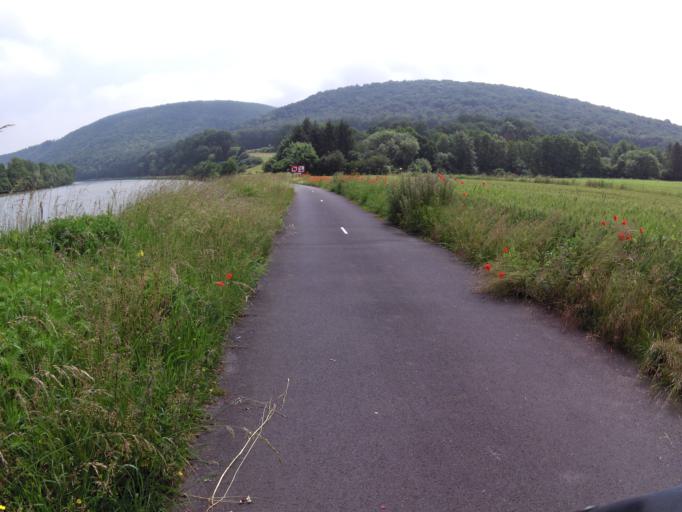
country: FR
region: Champagne-Ardenne
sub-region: Departement des Ardennes
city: Vireux-Wallerand
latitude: 50.0917
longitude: 4.7452
